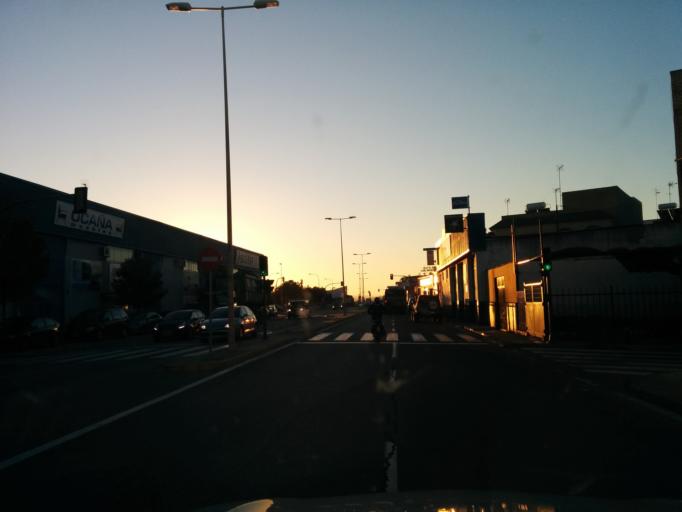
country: ES
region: Andalusia
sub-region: Provincia de Sevilla
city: Sevilla
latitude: 37.3763
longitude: -5.9319
